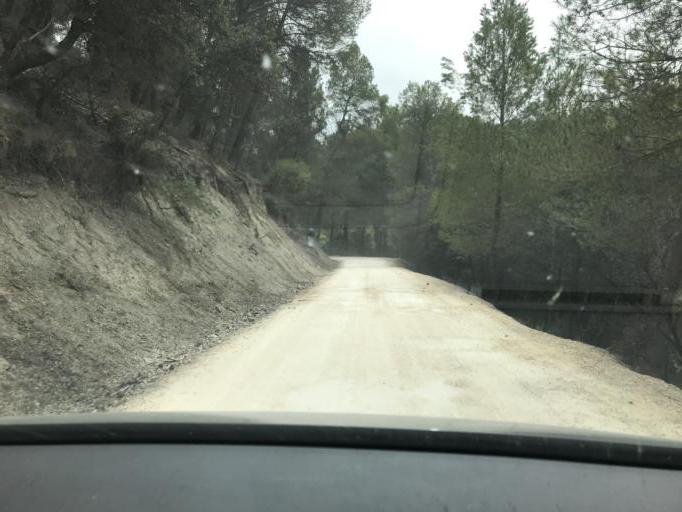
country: ES
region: Andalusia
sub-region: Provincia de Granada
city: Castril
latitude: 37.8415
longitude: -2.7745
